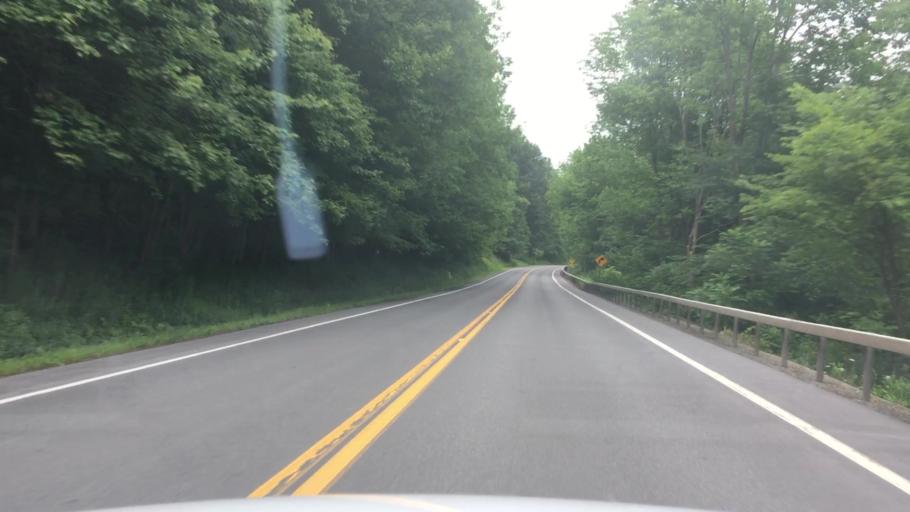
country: US
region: New York
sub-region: Otsego County
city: Otego
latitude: 42.4082
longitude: -75.1494
